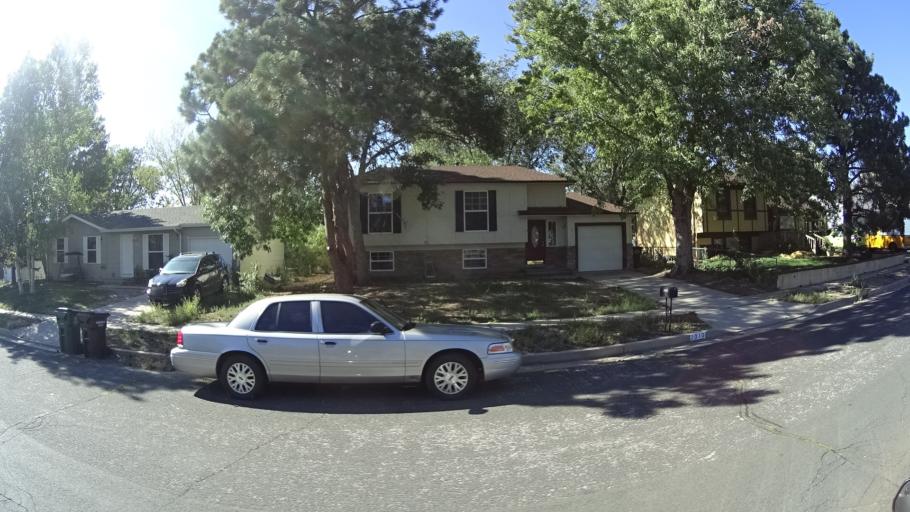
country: US
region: Colorado
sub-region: El Paso County
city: Stratmoor
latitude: 38.7949
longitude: -104.7537
